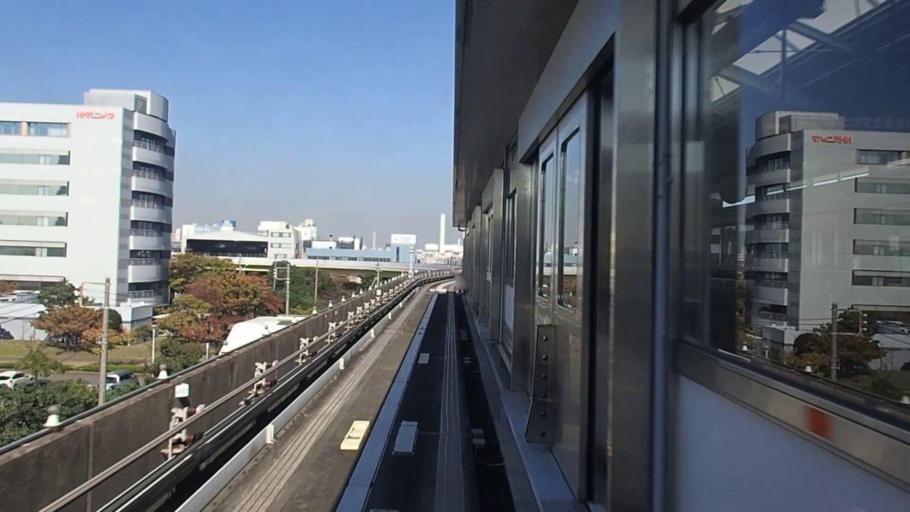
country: JP
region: Kanagawa
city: Yokosuka
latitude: 35.3438
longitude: 139.6501
